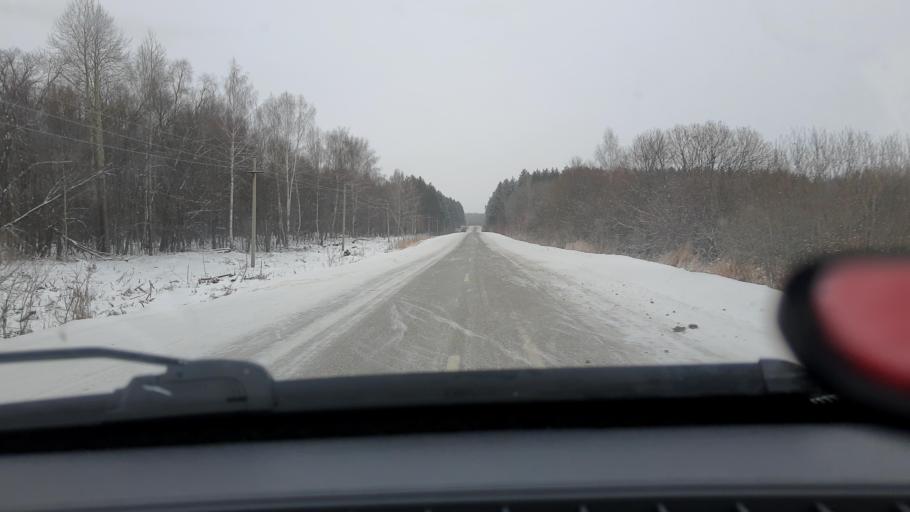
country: RU
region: Bashkortostan
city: Iglino
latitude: 54.6708
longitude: 56.4208
